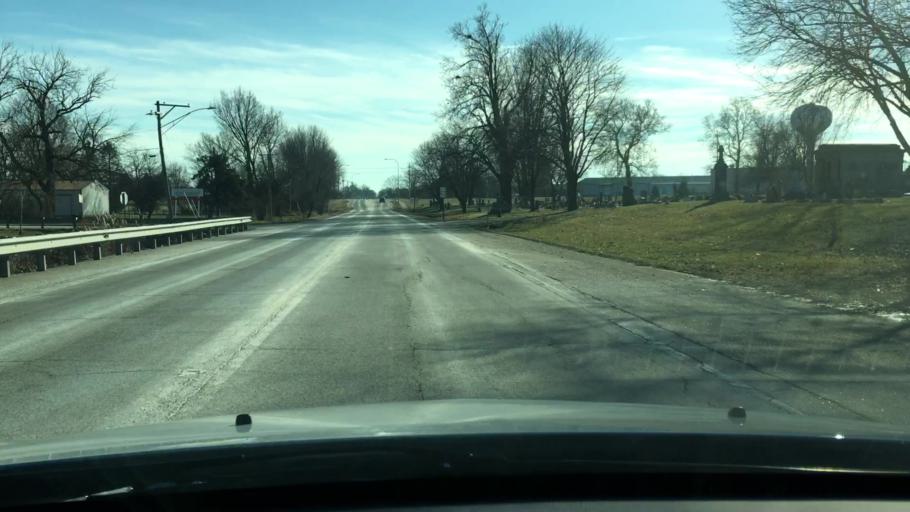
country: US
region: Illinois
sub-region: LaSalle County
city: Mendota
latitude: 41.5648
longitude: -89.1280
